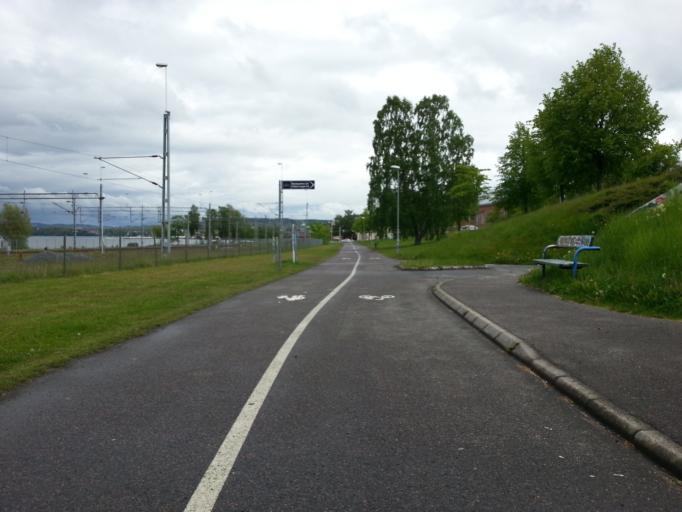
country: SE
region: Joenkoeping
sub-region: Jonkopings Kommun
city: Jonkoping
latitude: 57.7872
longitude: 14.1514
